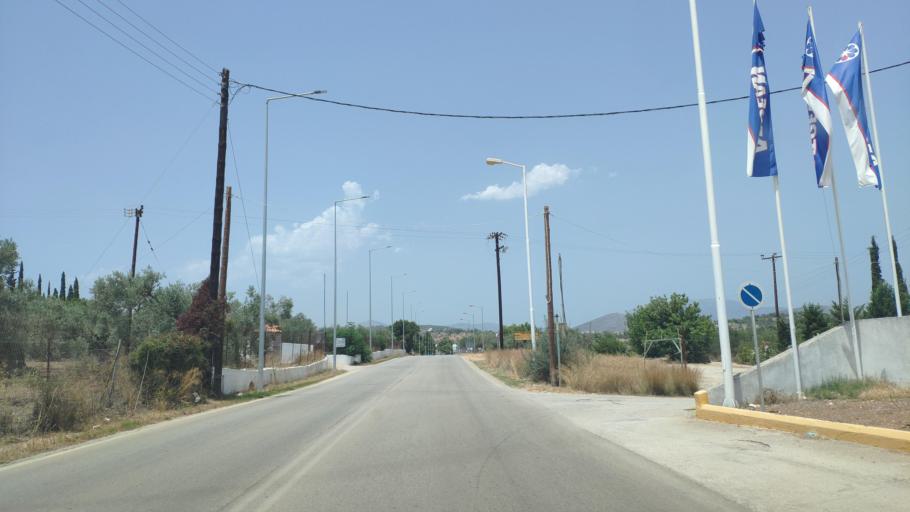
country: GR
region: Peloponnese
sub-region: Nomos Argolidos
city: Porto Cheli
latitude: 37.3440
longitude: 23.1576
